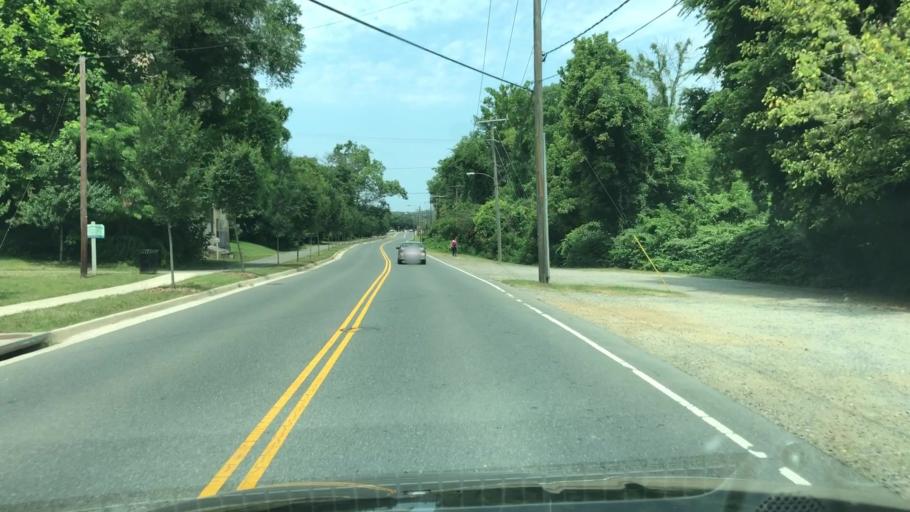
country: US
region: Virginia
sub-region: City of Fredericksburg
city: Fredericksburg
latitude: 38.3121
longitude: -77.4650
